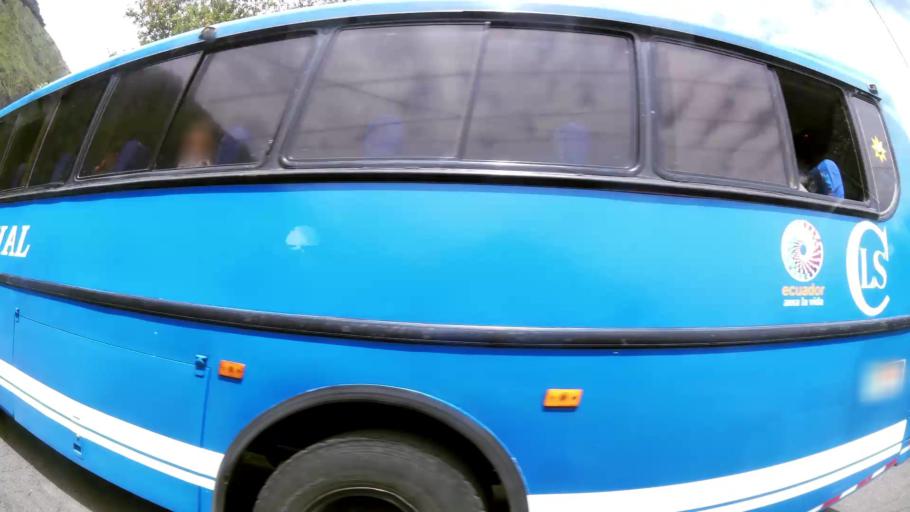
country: EC
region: Tungurahua
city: Banos
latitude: -1.3935
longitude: -78.4112
